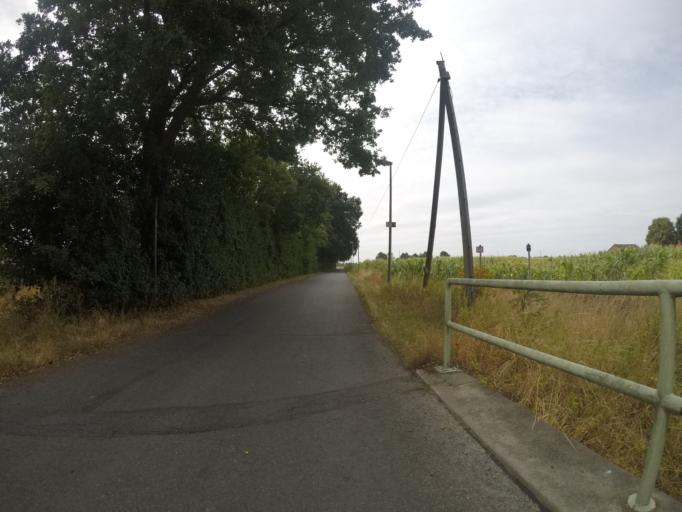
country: DE
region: North Rhine-Westphalia
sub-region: Regierungsbezirk Dusseldorf
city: Bocholt
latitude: 51.8553
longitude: 6.5836
